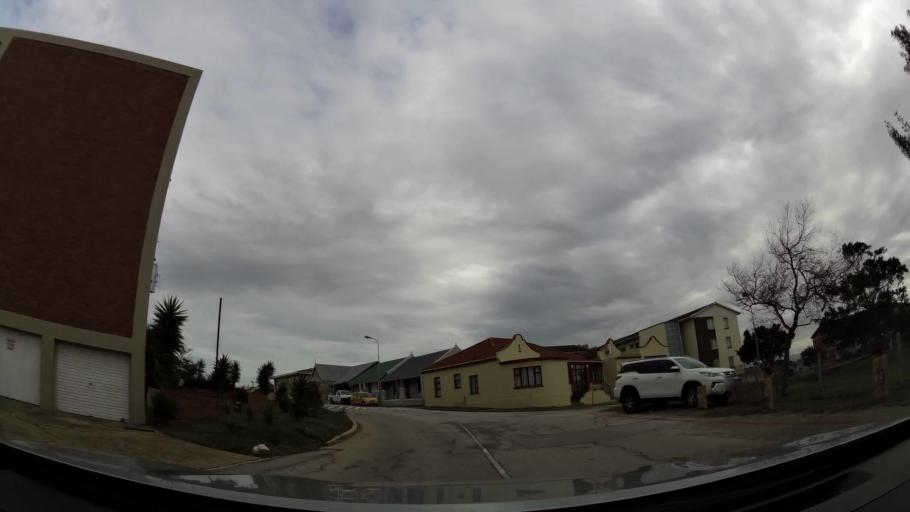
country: ZA
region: Eastern Cape
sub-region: Nelson Mandela Bay Metropolitan Municipality
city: Port Elizabeth
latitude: -33.9581
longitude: 25.6078
